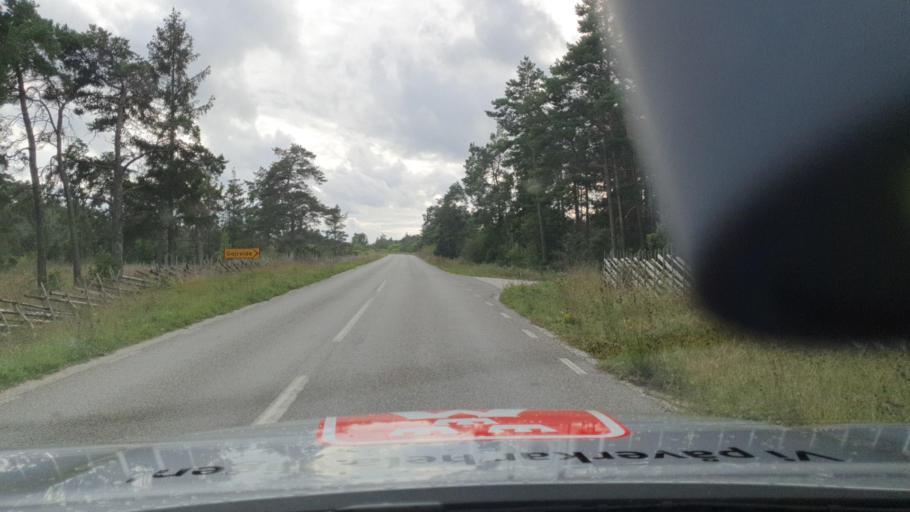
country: SE
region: Gotland
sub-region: Gotland
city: Slite
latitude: 57.6009
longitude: 18.7415
